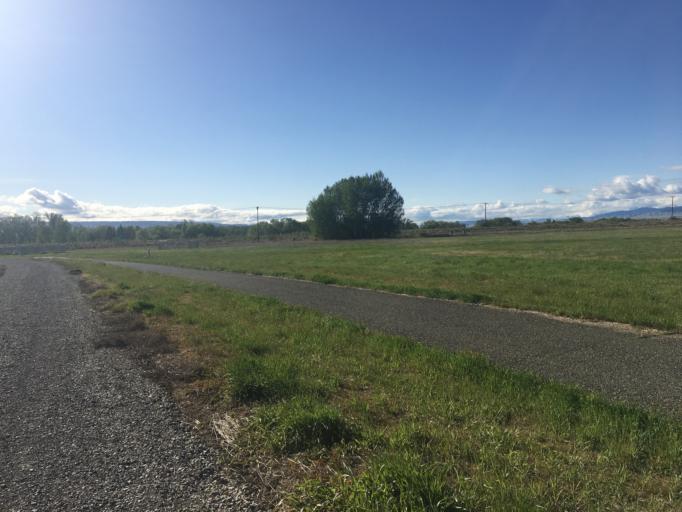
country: US
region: Washington
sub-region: Kittitas County
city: Ellensburg
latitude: 46.9908
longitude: -120.5680
